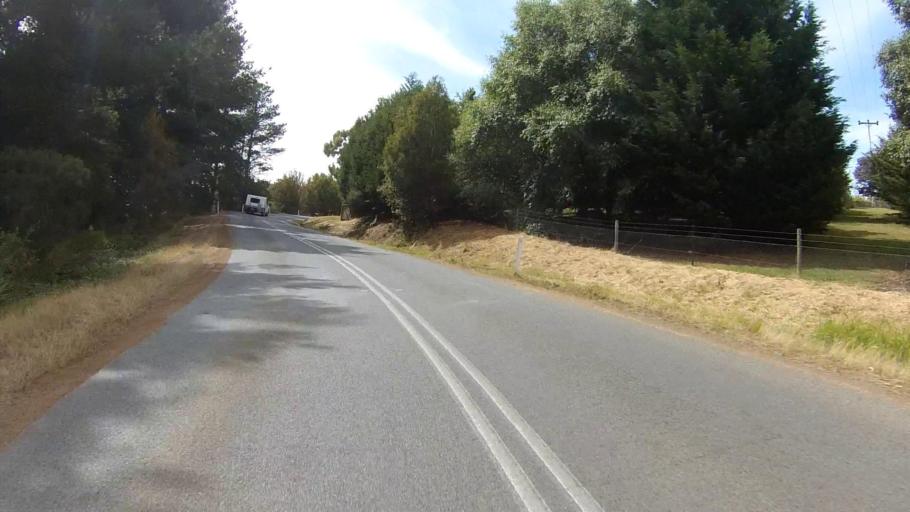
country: AU
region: Tasmania
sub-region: Kingborough
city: Kettering
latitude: -43.2065
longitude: 147.2539
